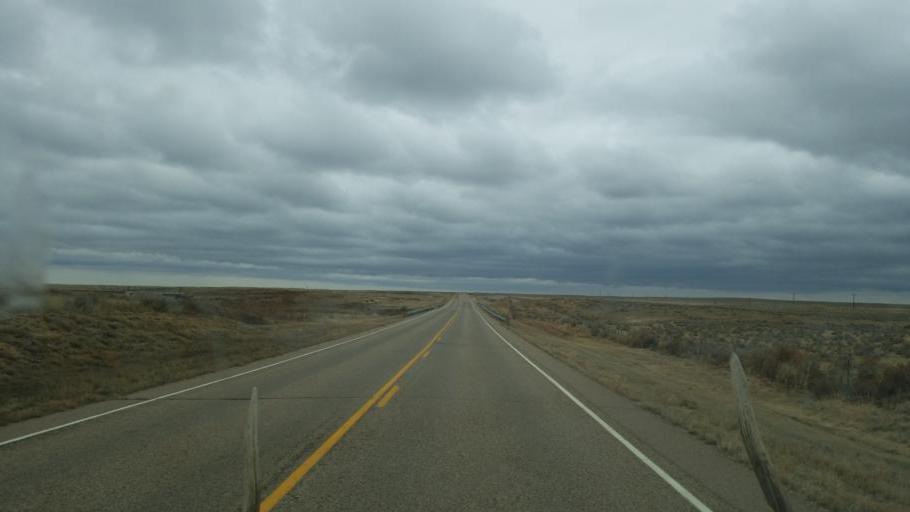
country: US
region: Colorado
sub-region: Kiowa County
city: Eads
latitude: 38.7883
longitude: -102.6835
